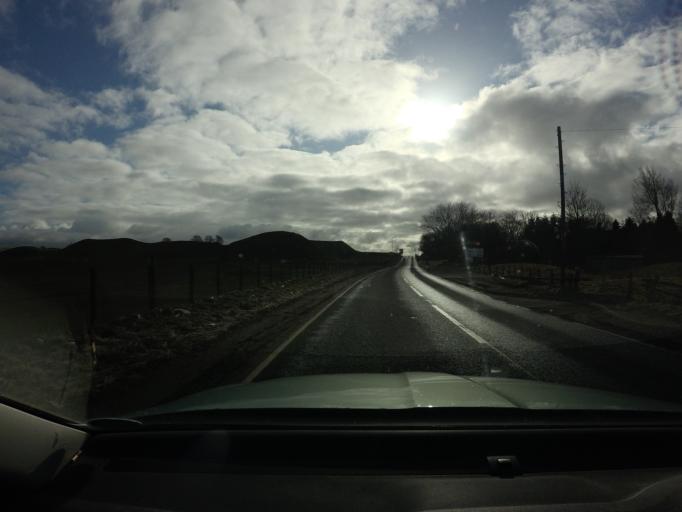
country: GB
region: Scotland
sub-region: South Lanarkshire
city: Forth
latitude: 55.7024
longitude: -3.6957
